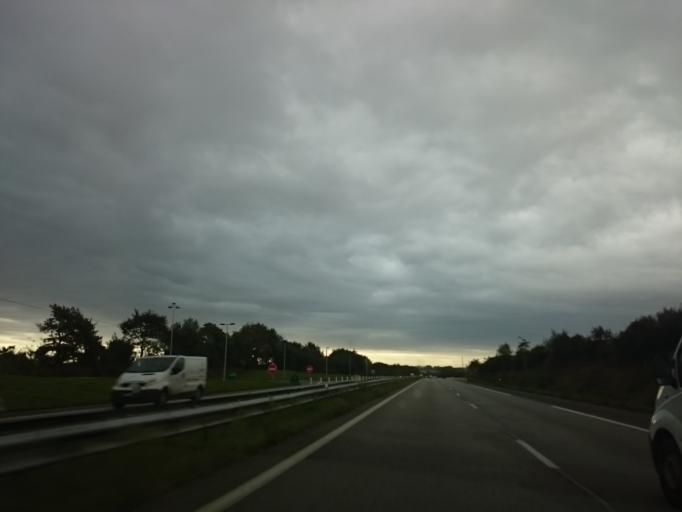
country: FR
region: Brittany
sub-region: Departement du Finistere
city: Landrevarzec
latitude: 48.0787
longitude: -4.0449
